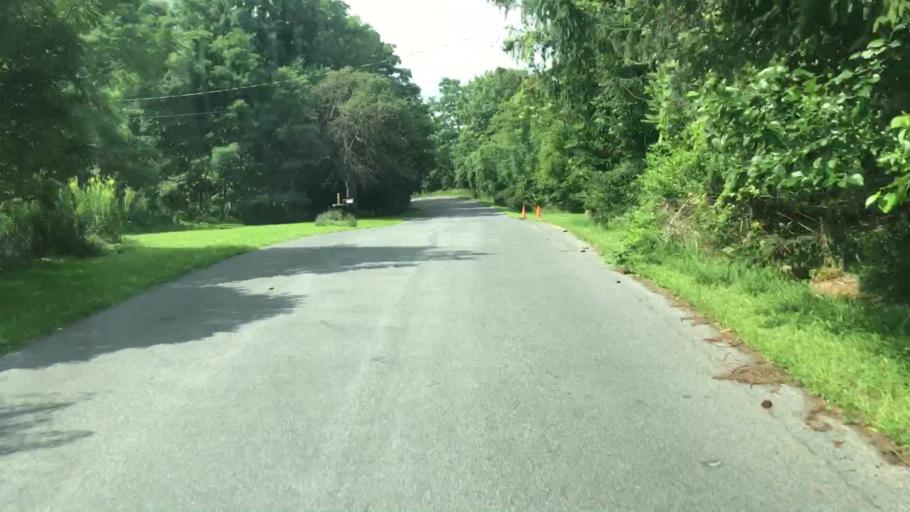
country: US
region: New York
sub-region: Onondaga County
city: Camillus
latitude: 43.0700
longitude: -76.3460
